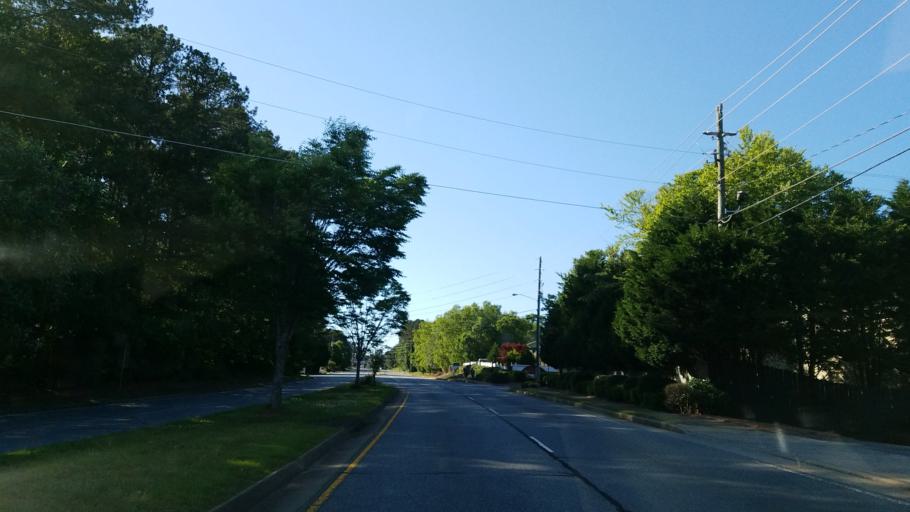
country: US
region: Georgia
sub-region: Cherokee County
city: Woodstock
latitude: 34.0757
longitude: -84.5715
